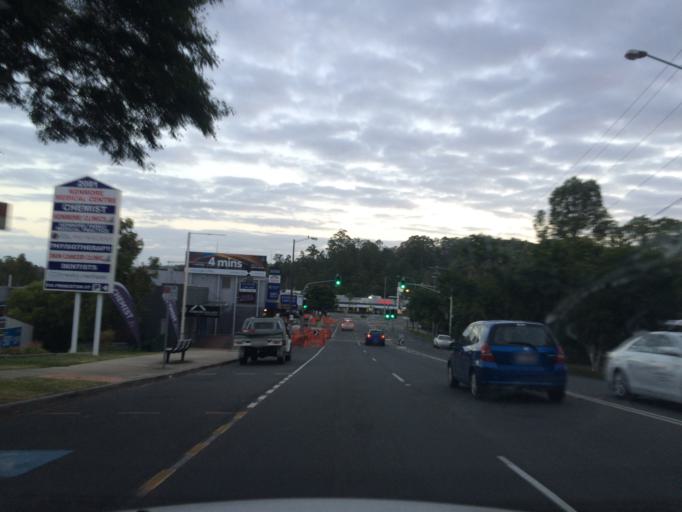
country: AU
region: Queensland
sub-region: Brisbane
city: Kenmore Hills
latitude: -27.5093
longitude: 152.9381
